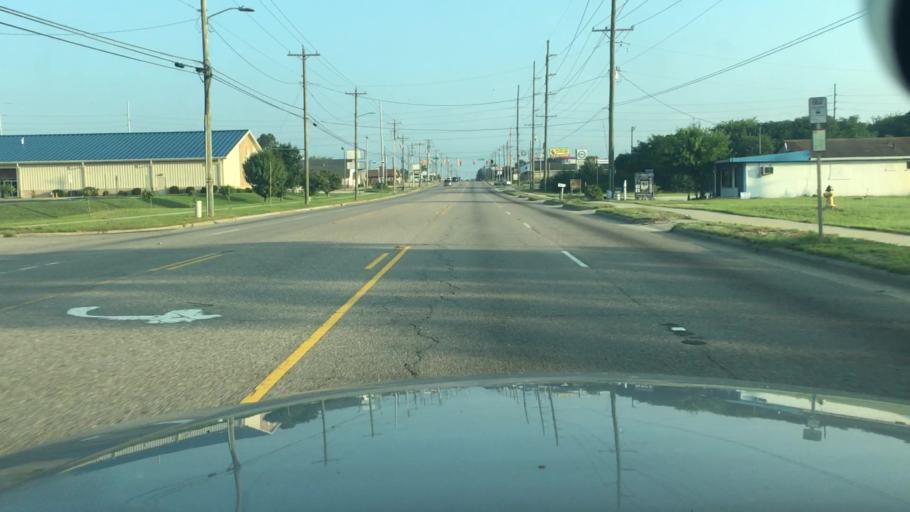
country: US
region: North Carolina
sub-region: Cumberland County
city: Spring Lake
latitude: 35.1101
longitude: -78.9264
